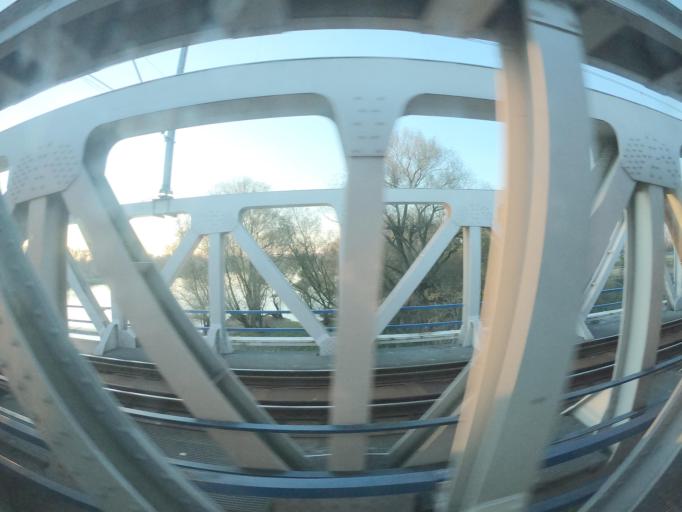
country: PL
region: Lubusz
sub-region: Powiat gorzowski
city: Kostrzyn nad Odra
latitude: 52.5852
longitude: 14.6439
